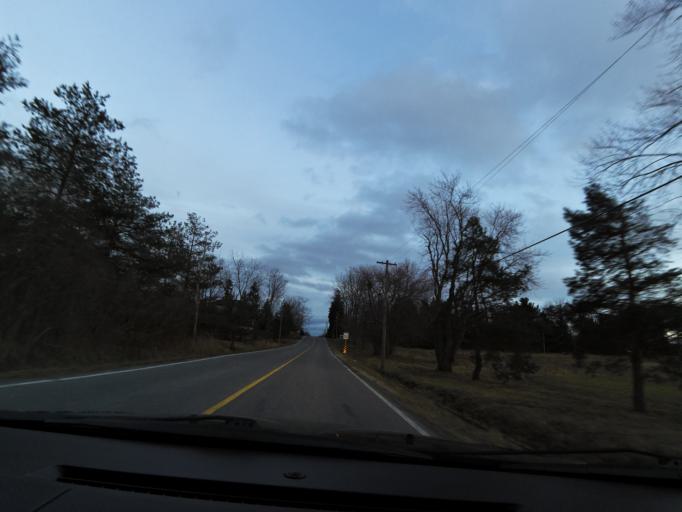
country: CA
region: Ontario
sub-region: Halton
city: Milton
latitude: 43.4435
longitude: -79.8963
